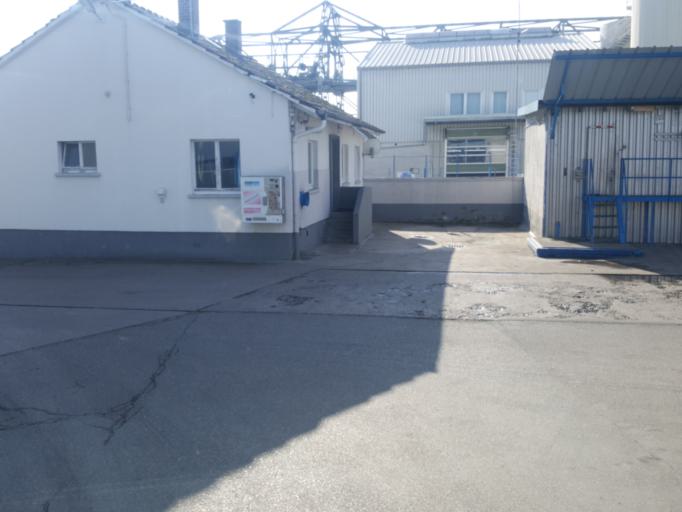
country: FR
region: Alsace
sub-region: Departement du Haut-Rhin
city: Huningue
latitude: 47.5951
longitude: 7.5940
